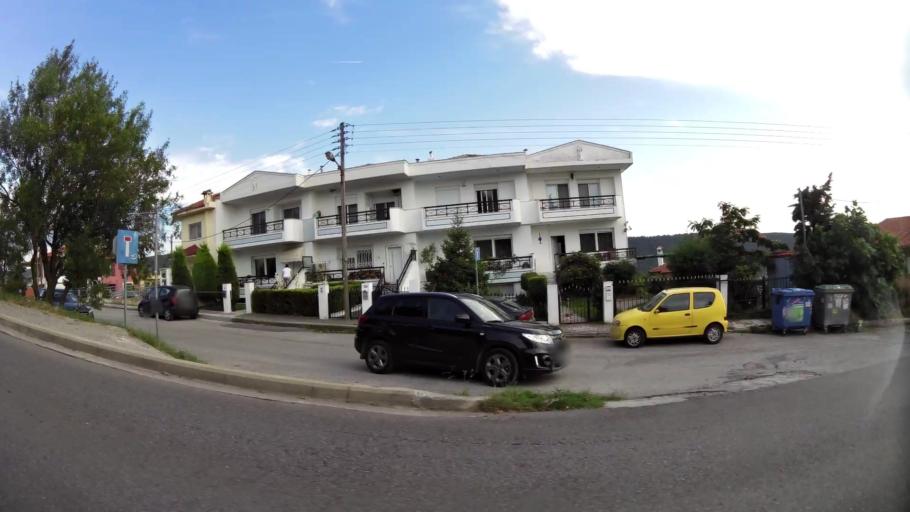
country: GR
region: Central Macedonia
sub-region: Nomos Thessalonikis
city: Pefka
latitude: 40.6602
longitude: 22.9954
